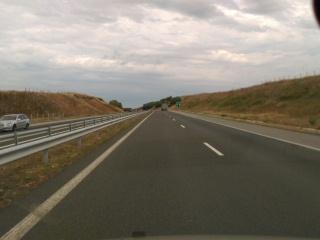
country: BG
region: Yambol
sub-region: Obshtina Yambol
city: Yambol
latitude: 42.5415
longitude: 26.4651
